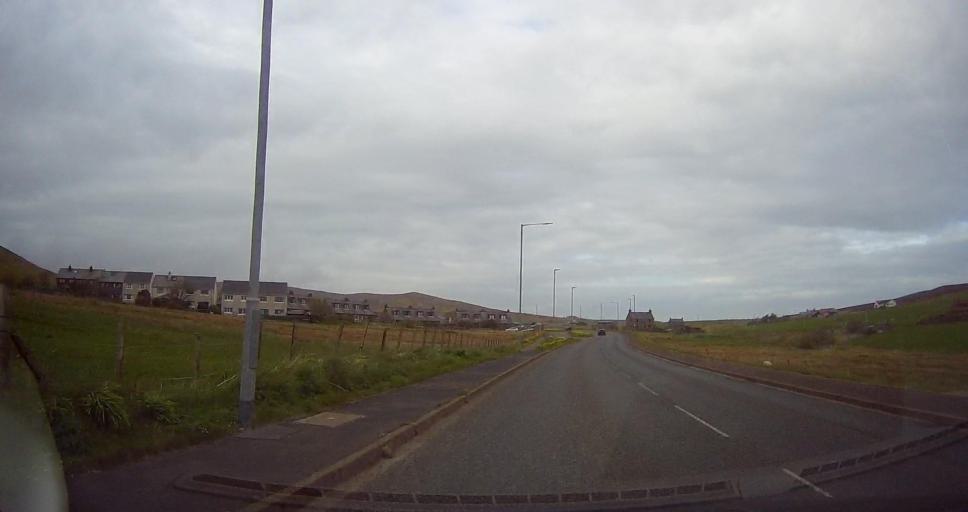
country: GB
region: Scotland
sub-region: Shetland Islands
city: Sandwick
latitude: 60.0517
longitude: -1.2268
